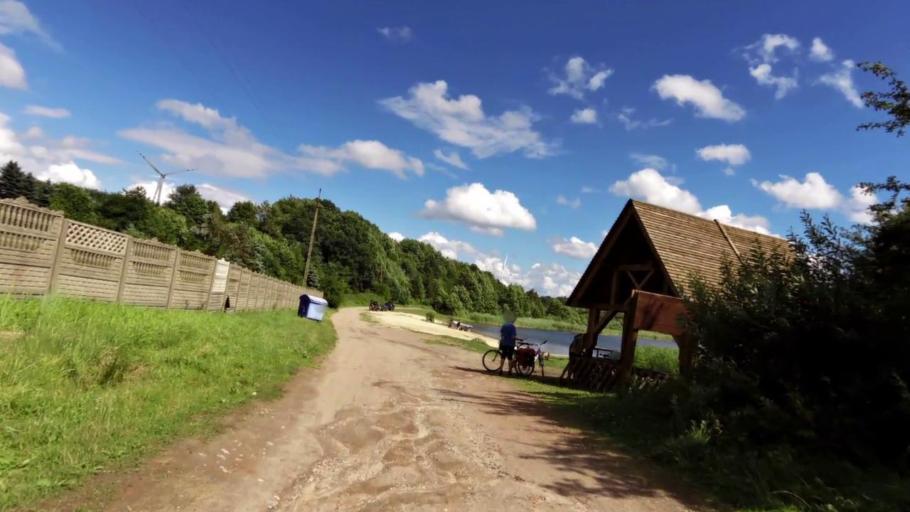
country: PL
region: West Pomeranian Voivodeship
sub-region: Powiat slawienski
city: Slawno
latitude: 54.5110
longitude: 16.7085
